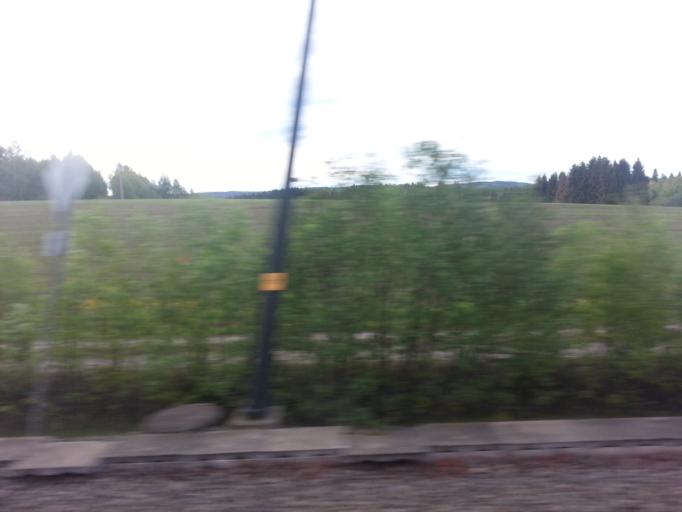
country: NO
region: Akershus
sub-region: Eidsvoll
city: Raholt
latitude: 60.2918
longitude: 11.1752
